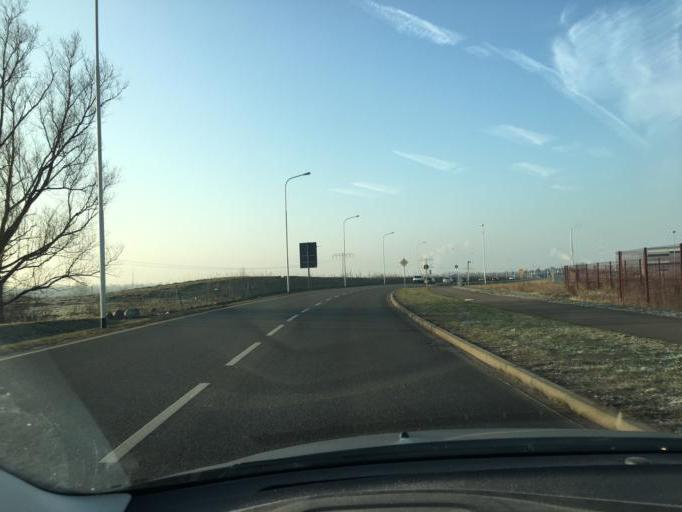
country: DE
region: Saxony-Anhalt
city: Halle (Saale)
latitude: 51.4759
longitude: 12.0169
